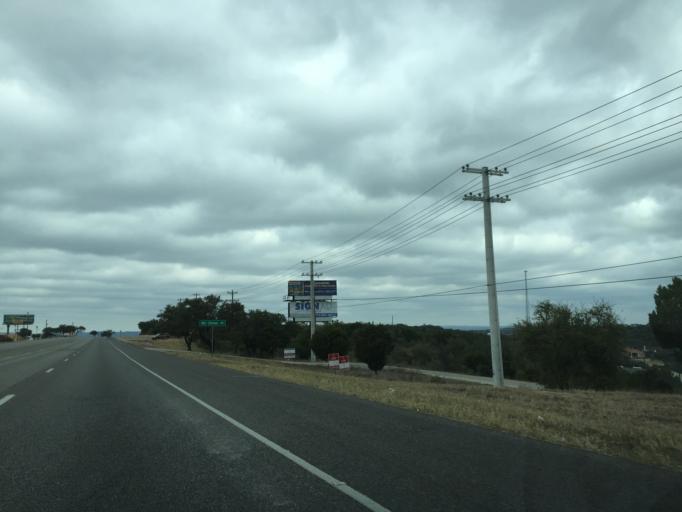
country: US
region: Texas
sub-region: Travis County
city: Briarcliff
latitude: 30.3551
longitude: -98.0662
